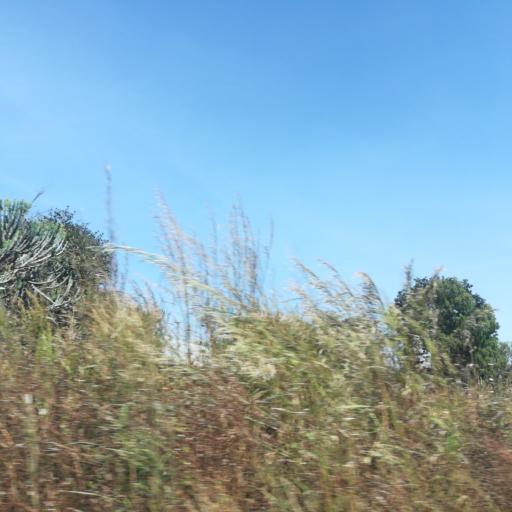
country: NG
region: Plateau
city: Bukuru
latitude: 9.7575
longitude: 8.8744
